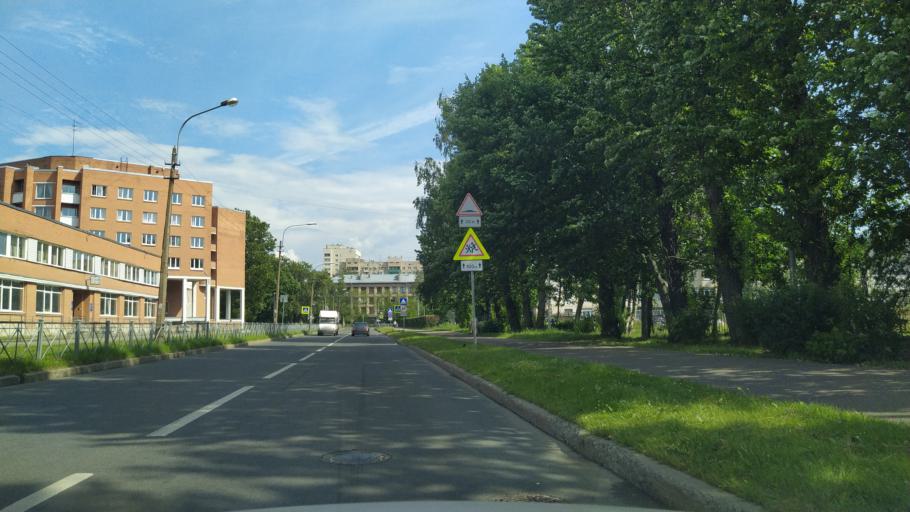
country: RU
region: St.-Petersburg
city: Kushelevka
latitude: 60.0000
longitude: 30.3754
